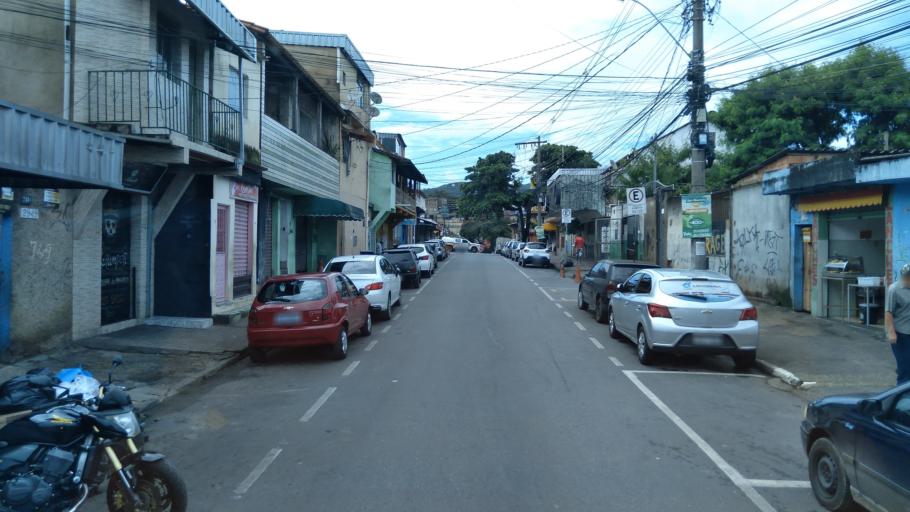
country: BR
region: Minas Gerais
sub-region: Belo Horizonte
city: Belo Horizonte
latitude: -19.9076
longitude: -43.8918
